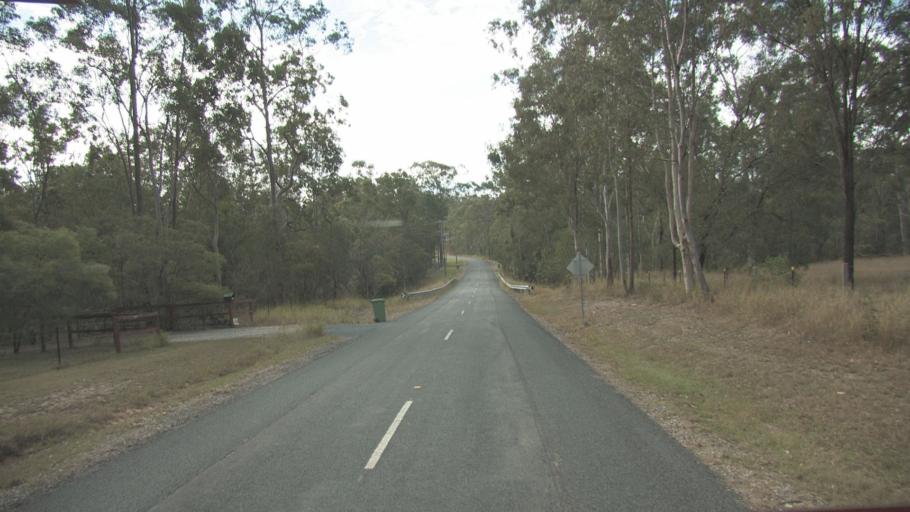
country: AU
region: Queensland
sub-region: Logan
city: North Maclean
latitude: -27.7584
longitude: 152.9724
